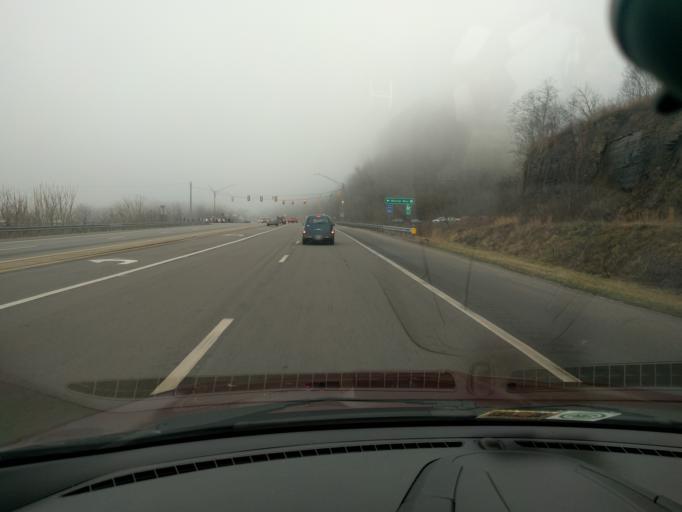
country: US
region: West Virginia
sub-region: Kanawha County
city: Chesapeake
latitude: 38.2103
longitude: -81.5089
